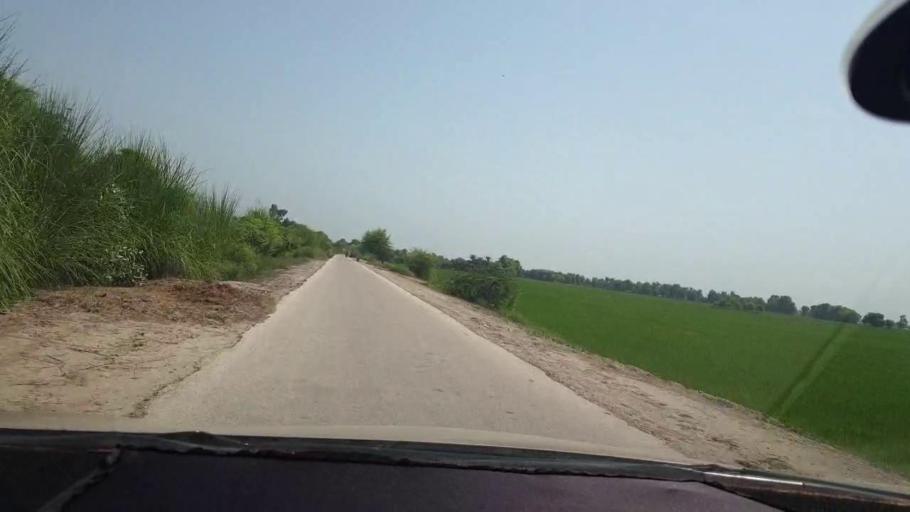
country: PK
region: Sindh
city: Kambar
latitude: 27.5160
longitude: 68.0106
